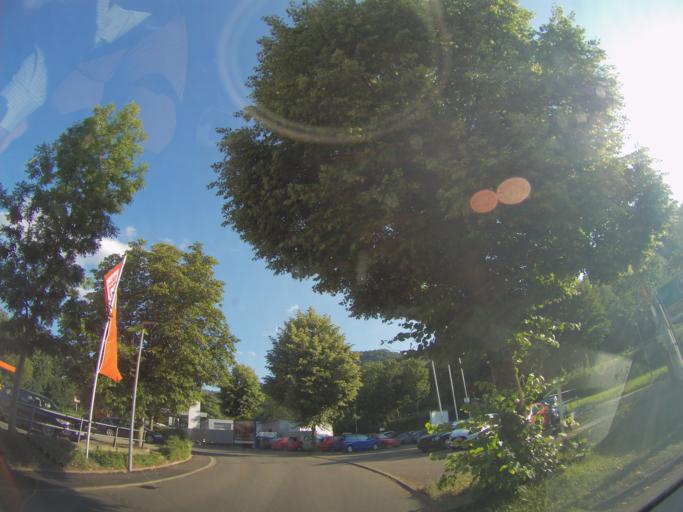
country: DE
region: Baden-Wuerttemberg
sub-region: Regierungsbezirk Stuttgart
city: Kuchen
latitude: 48.6451
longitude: 9.7900
